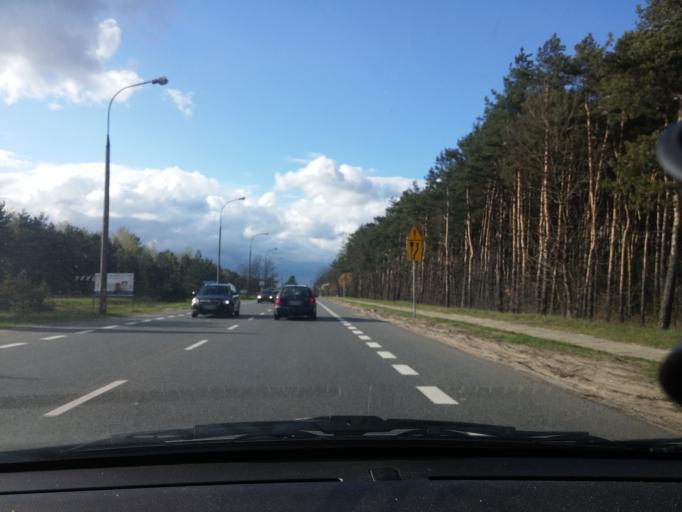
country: PL
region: Masovian Voivodeship
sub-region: Warszawa
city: Wawer
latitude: 52.1967
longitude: 21.1768
